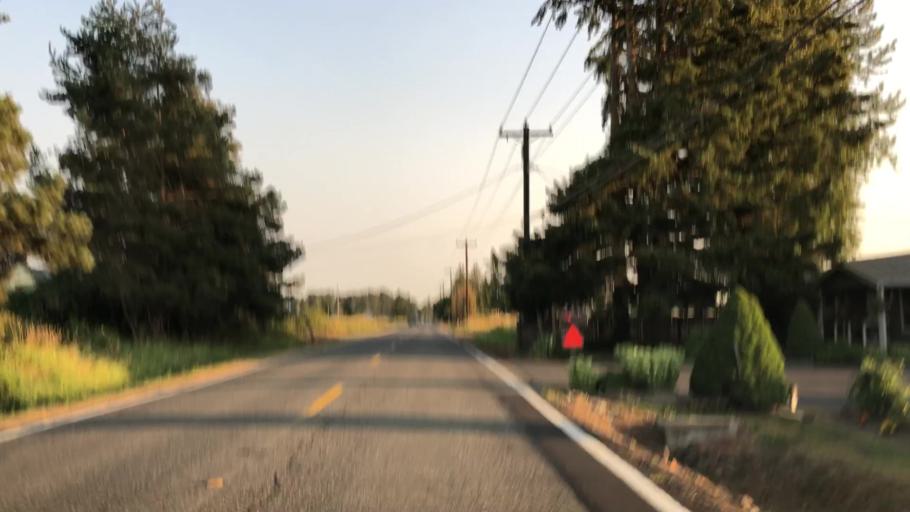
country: US
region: Washington
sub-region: Snohomish County
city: Smokey Point
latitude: 48.1375
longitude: -122.1619
